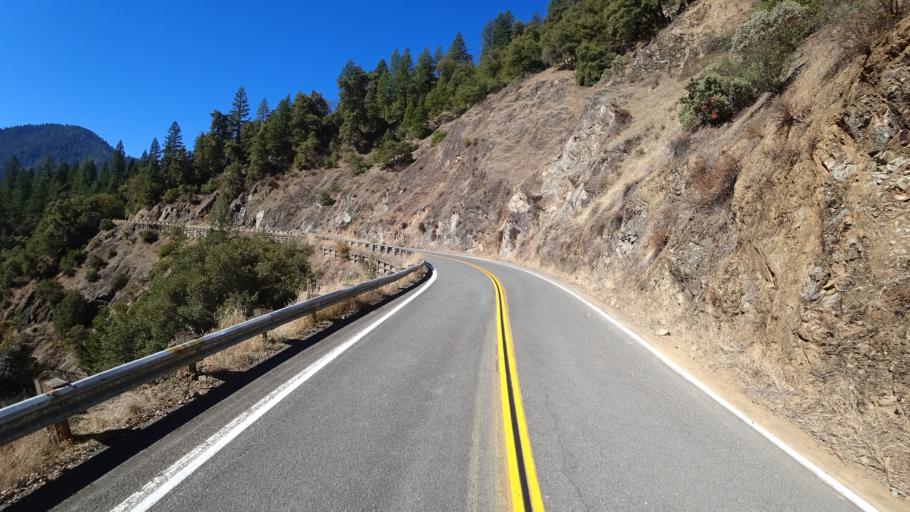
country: US
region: California
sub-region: Siskiyou County
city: Happy Camp
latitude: 41.3787
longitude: -123.4388
